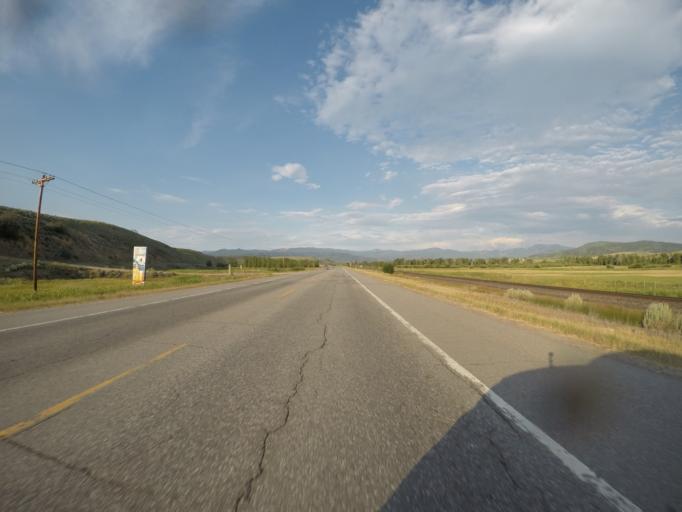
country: US
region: Colorado
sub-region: Routt County
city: Steamboat Springs
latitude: 40.4910
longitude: -106.9572
